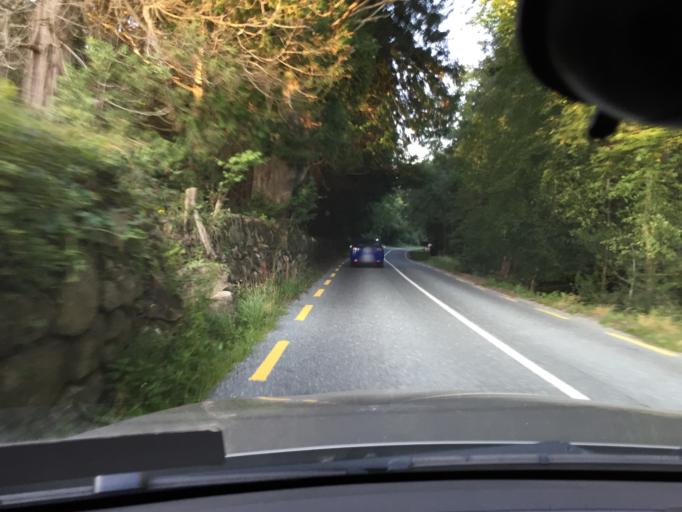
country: IE
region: Leinster
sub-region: Wicklow
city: Rathdrum
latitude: 53.0200
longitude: -6.2744
